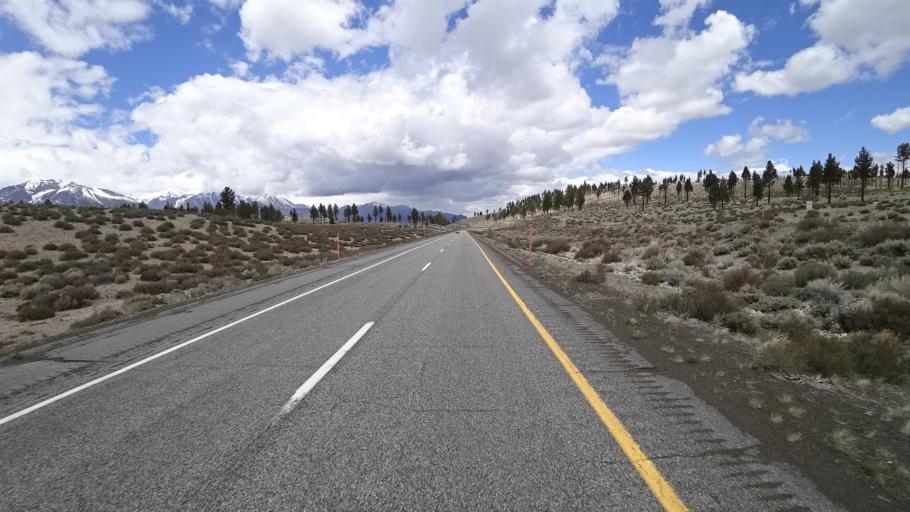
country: US
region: California
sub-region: Mono County
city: Mammoth Lakes
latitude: 37.8223
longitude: -119.0625
